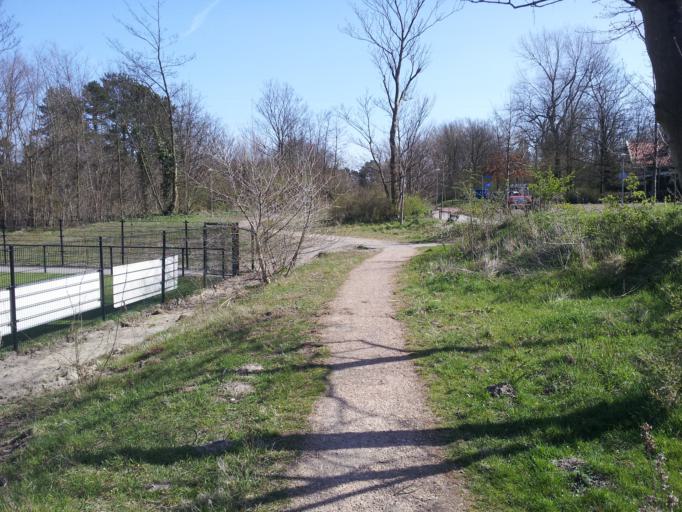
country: NL
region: South Holland
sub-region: Gemeente Rotterdam
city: Hoek van Holland
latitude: 51.9828
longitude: 4.1246
